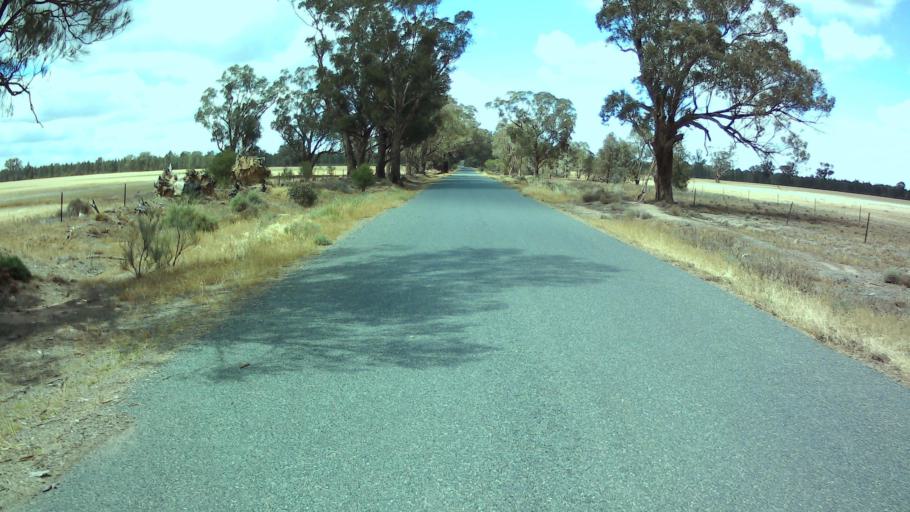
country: AU
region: New South Wales
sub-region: Weddin
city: Grenfell
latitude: -33.8930
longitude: 147.9222
